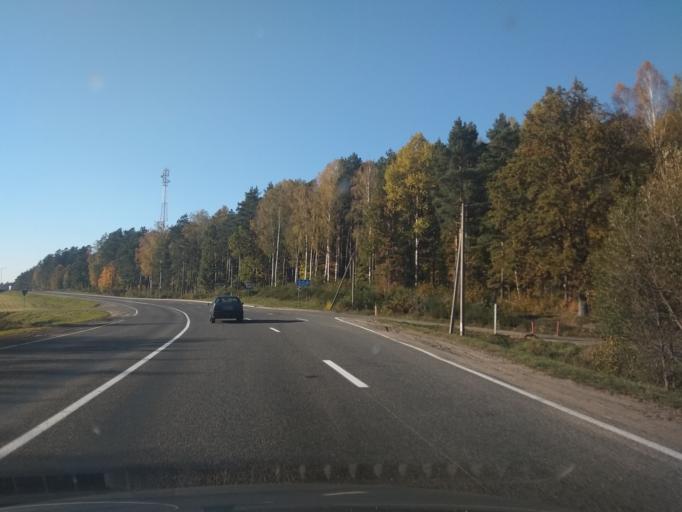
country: BY
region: Grodnenskaya
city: Vyalikaya Byerastavitsa
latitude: 53.1200
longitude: 23.9196
